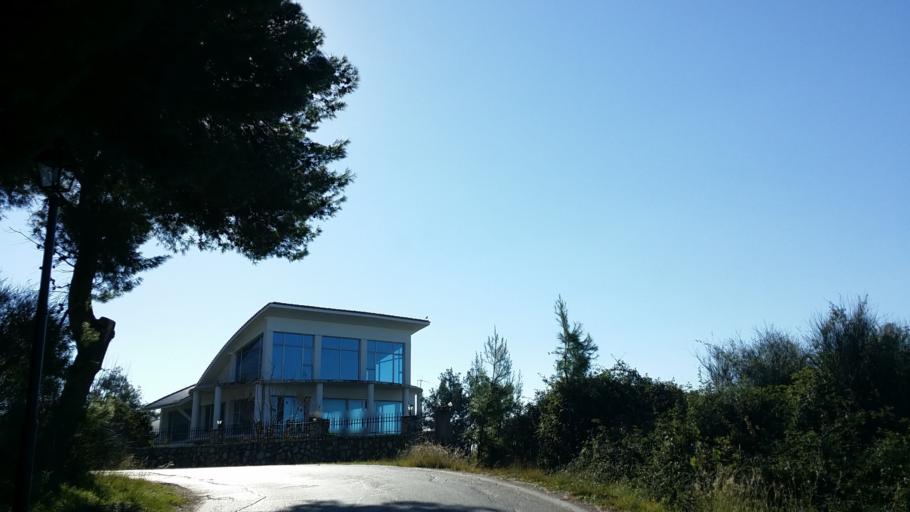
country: GR
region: West Greece
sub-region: Nomos Aitolias kai Akarnanias
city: Palairos
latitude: 38.7741
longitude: 20.8808
